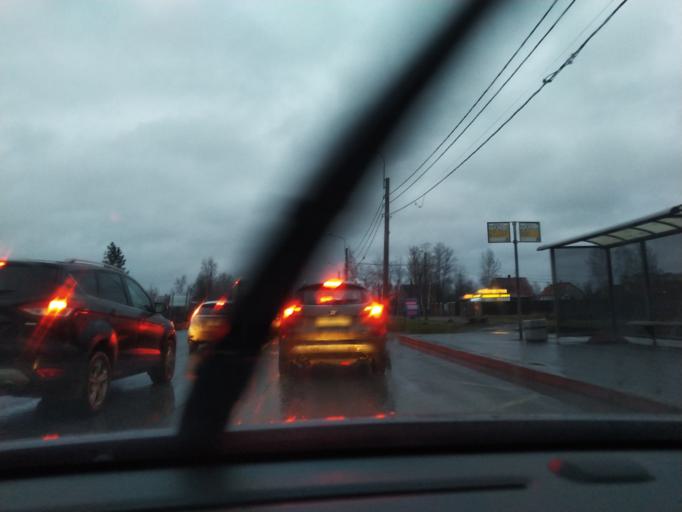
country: RU
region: St.-Petersburg
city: Uritsk
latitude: 59.8136
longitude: 30.1730
